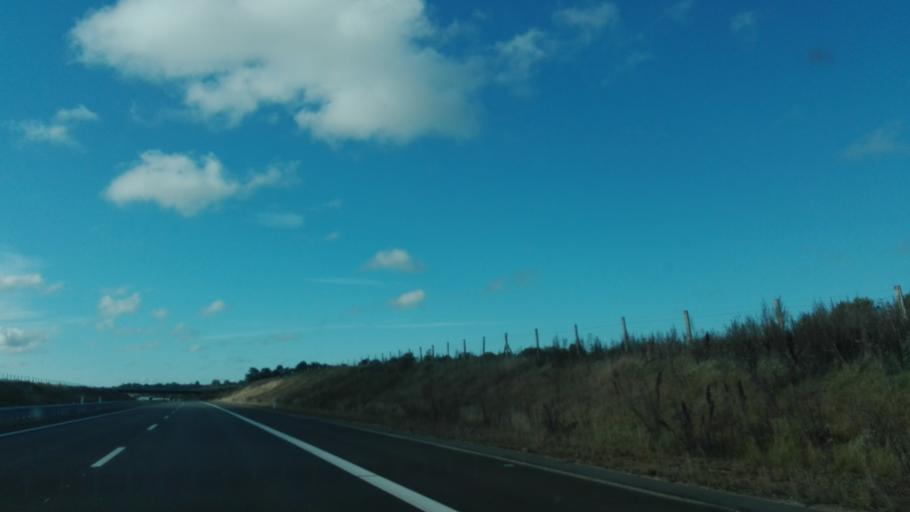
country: DK
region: Central Jutland
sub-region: Silkeborg Kommune
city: Silkeborg
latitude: 56.1940
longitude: 9.5005
